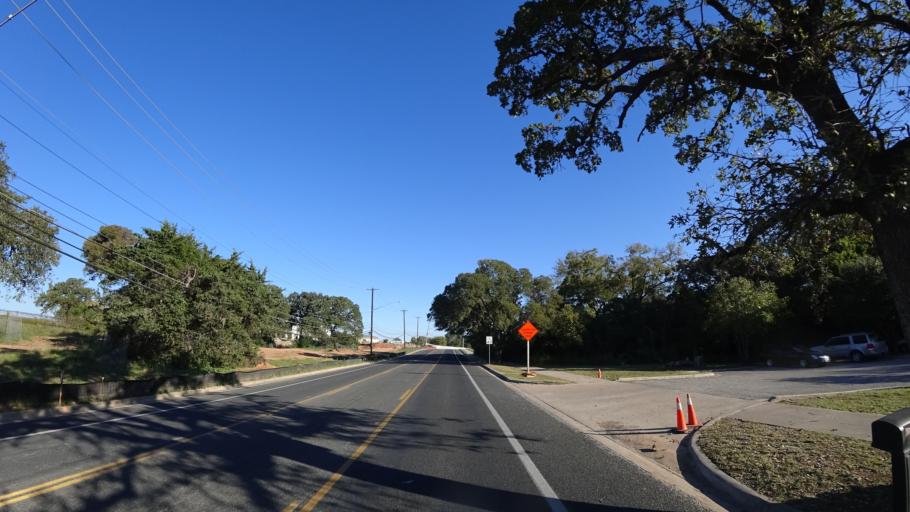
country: US
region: Texas
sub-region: Travis County
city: Austin
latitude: 30.2928
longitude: -97.6893
